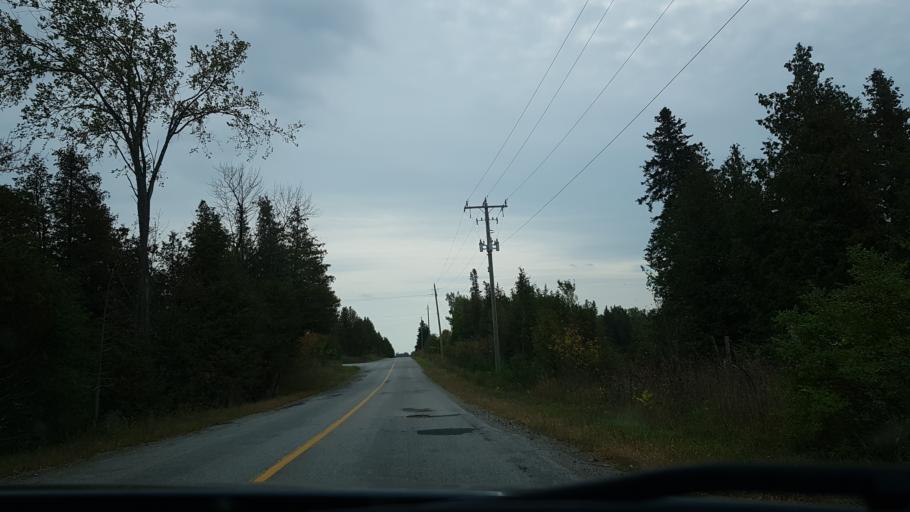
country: CA
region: Ontario
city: Orillia
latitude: 44.6448
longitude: -78.9622
